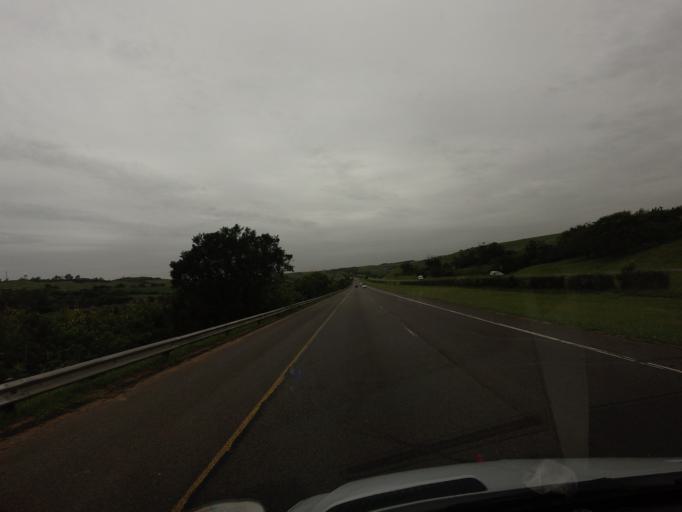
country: ZA
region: KwaZulu-Natal
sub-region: eThekwini Metropolitan Municipality
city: Durban
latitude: -29.6917
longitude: 31.0826
